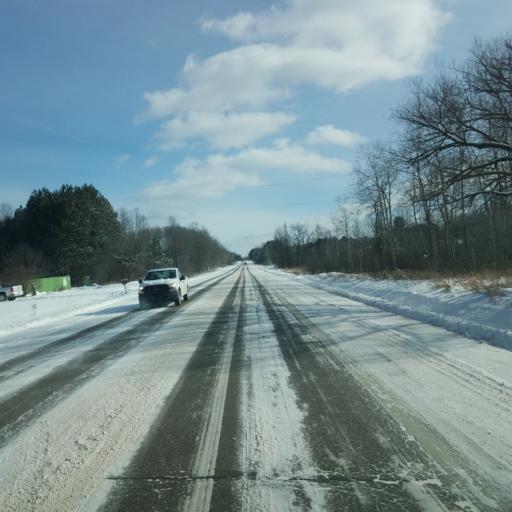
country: US
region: Michigan
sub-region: Osceola County
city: Evart
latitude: 43.9008
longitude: -85.1370
